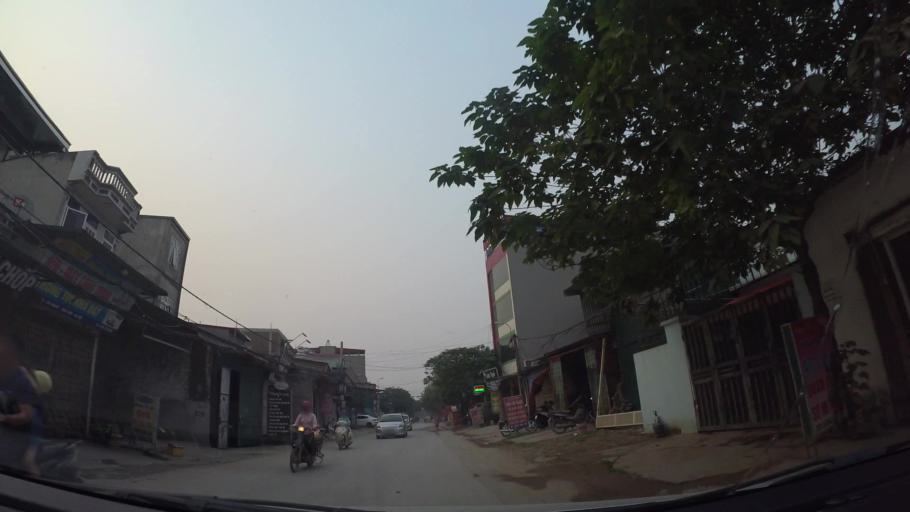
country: VN
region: Ha Noi
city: Ha Dong
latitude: 20.9914
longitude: 105.7247
